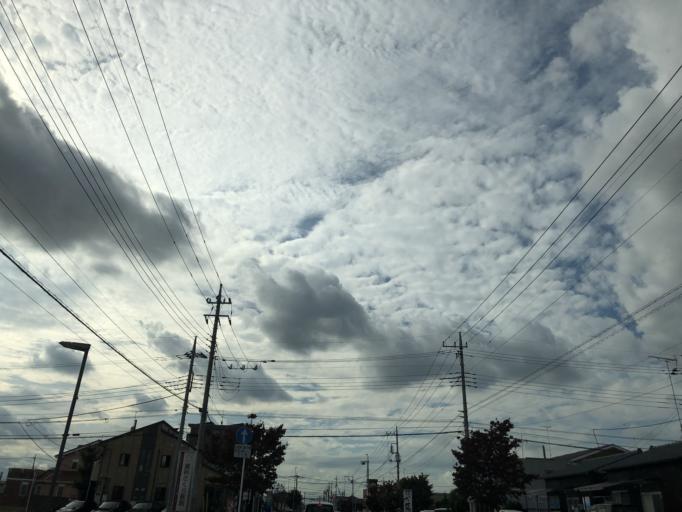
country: JP
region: Tochigi
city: Sano
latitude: 36.2996
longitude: 139.5965
